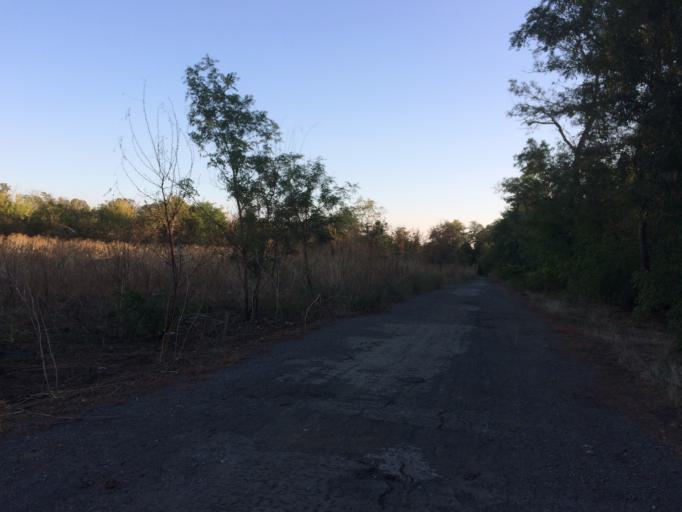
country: RU
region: Rostov
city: Gigant
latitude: 46.5121
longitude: 41.1943
